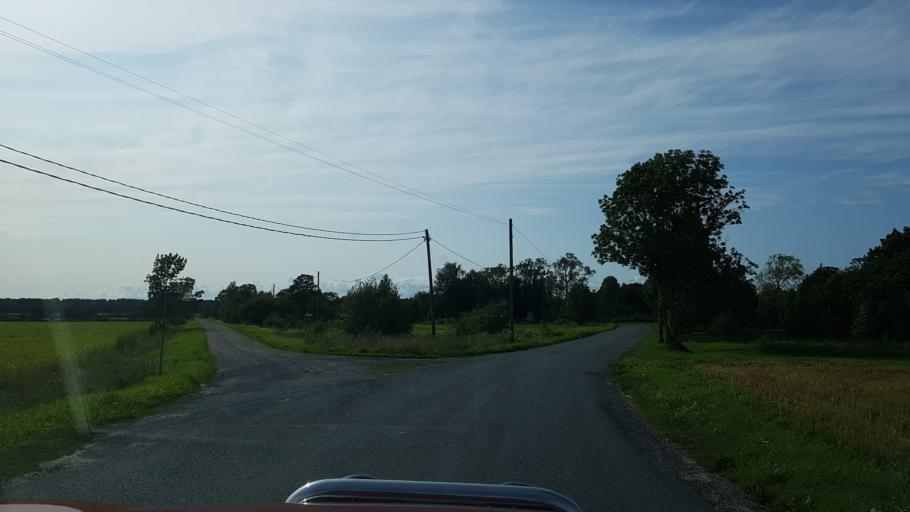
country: EE
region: Laeaene
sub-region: Lihula vald
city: Lihula
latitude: 58.4481
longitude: 24.0010
